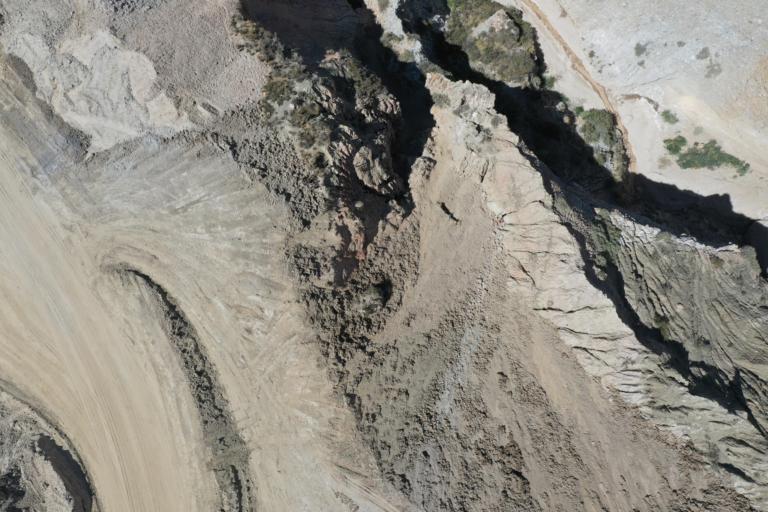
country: BO
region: La Paz
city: La Paz
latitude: -16.5588
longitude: -68.1301
